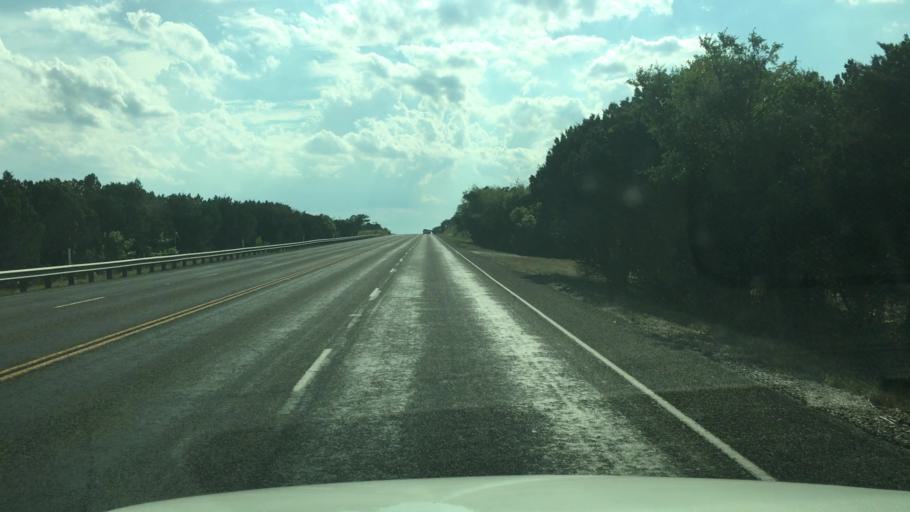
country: US
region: Texas
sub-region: Blanco County
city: Johnson City
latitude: 30.2094
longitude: -98.2942
